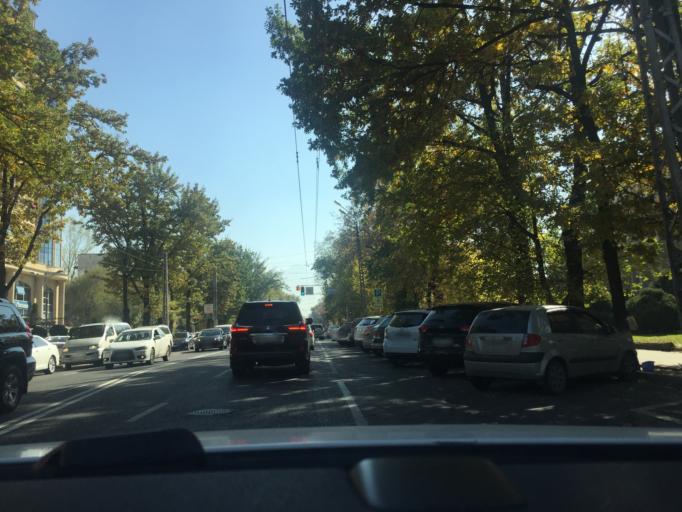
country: KZ
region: Almaty Qalasy
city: Almaty
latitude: 43.2461
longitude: 76.9031
